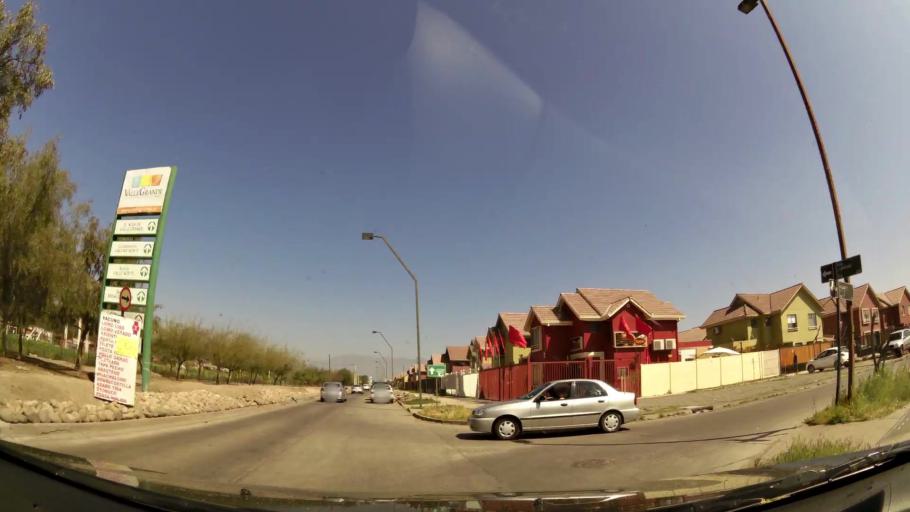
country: CL
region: Santiago Metropolitan
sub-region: Provincia de Chacabuco
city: Chicureo Abajo
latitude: -33.3249
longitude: -70.7495
